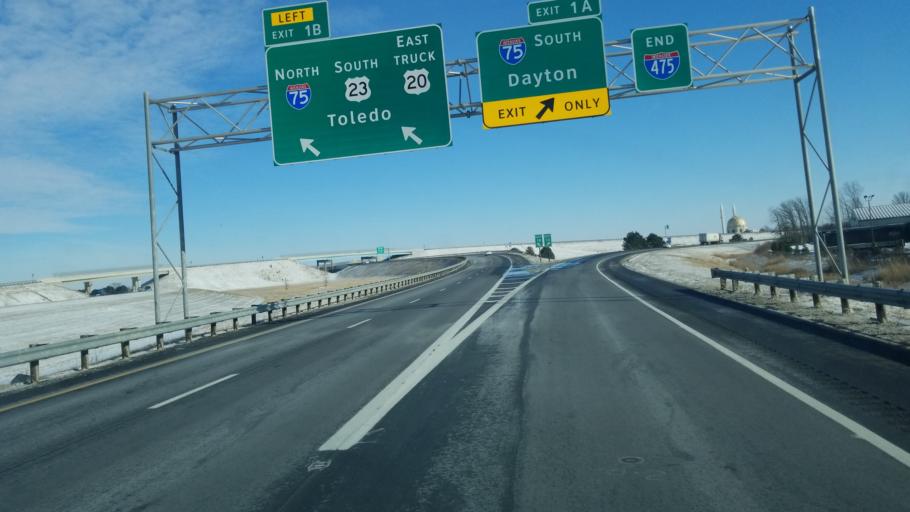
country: US
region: Ohio
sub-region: Wood County
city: Perrysburg
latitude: 41.5318
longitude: -83.6269
